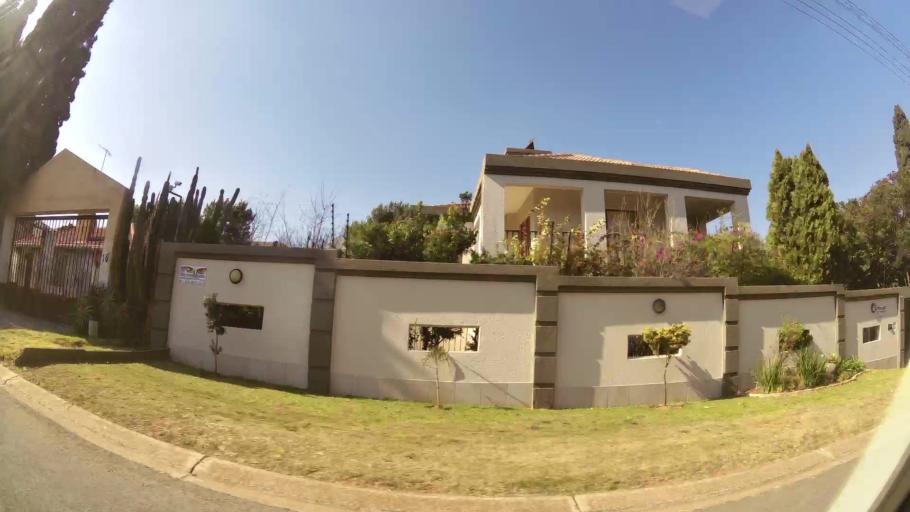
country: ZA
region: Gauteng
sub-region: City of Johannesburg Metropolitan Municipality
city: Johannesburg
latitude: -26.2662
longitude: 28.0357
